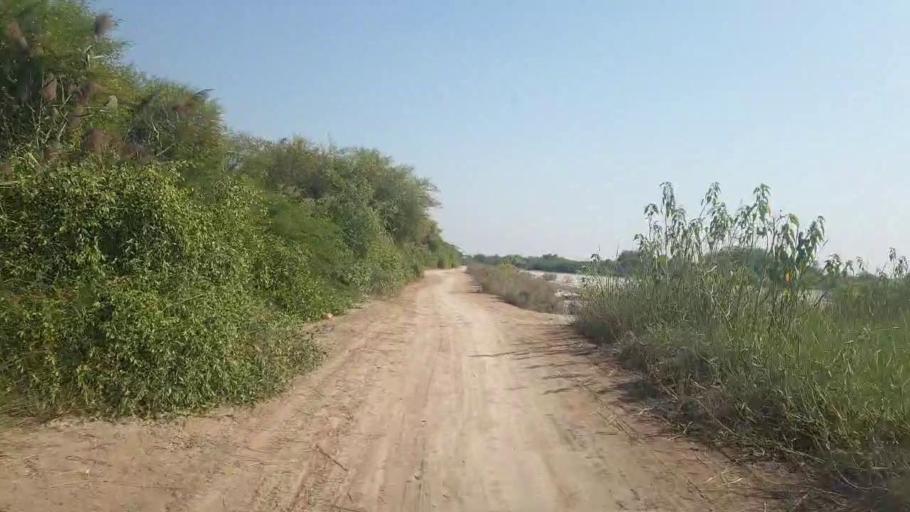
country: PK
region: Sindh
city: Badin
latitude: 24.7138
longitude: 68.8860
